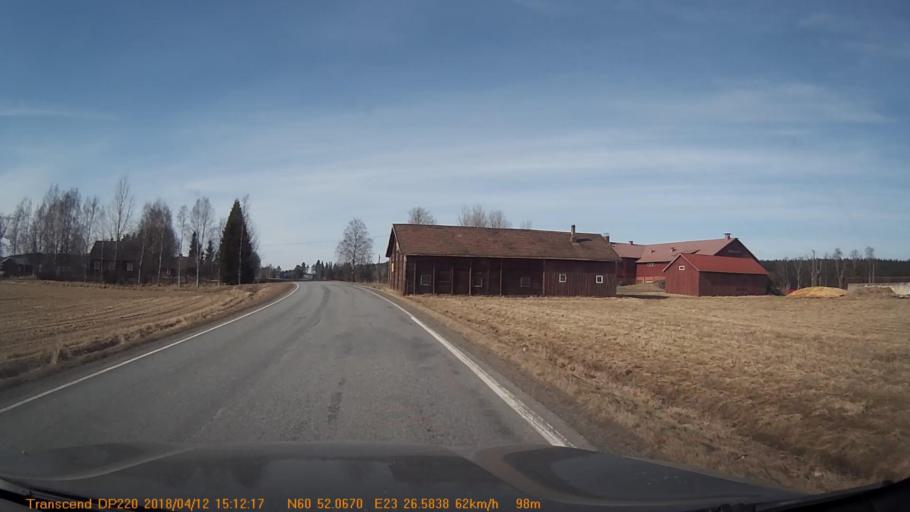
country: FI
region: Haeme
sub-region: Forssa
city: Jokioinen
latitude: 60.8679
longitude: 23.4430
